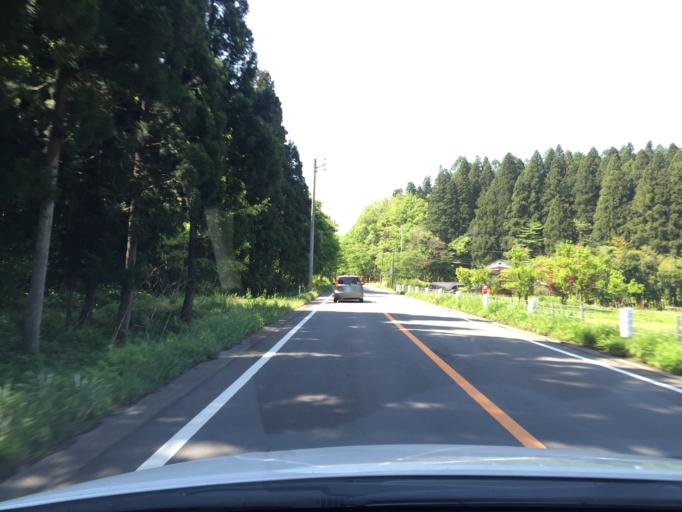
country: JP
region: Niigata
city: Muramatsu
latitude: 37.6573
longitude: 139.1376
